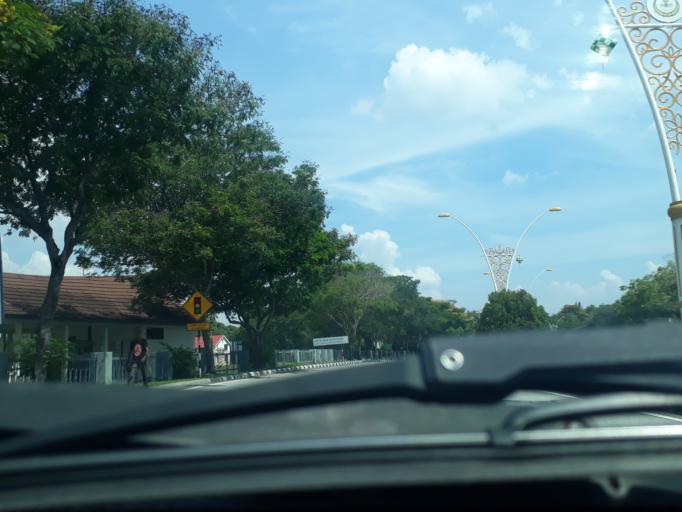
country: MY
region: Perak
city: Ipoh
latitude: 4.5947
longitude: 101.1191
